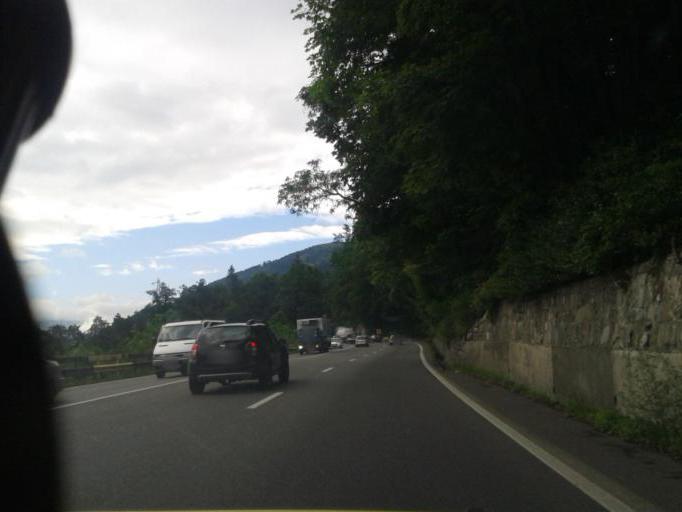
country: RO
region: Prahova
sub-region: Comuna Comarnic
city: Posada
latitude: 45.2797
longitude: 25.6207
